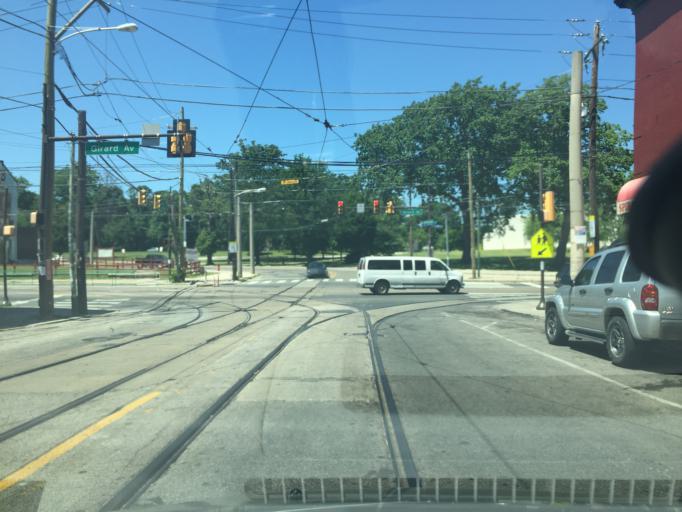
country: US
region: Pennsylvania
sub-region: Montgomery County
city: Bala-Cynwyd
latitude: 39.9738
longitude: -75.2043
